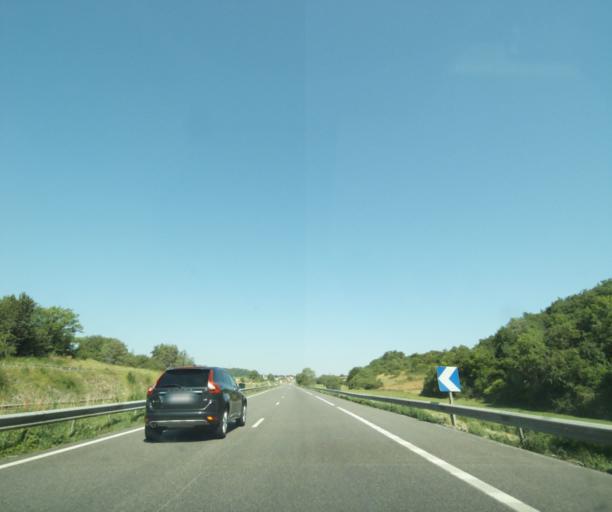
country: FR
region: Lorraine
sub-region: Departement de la Meuse
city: Vacon
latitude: 48.6948
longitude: 5.5477
